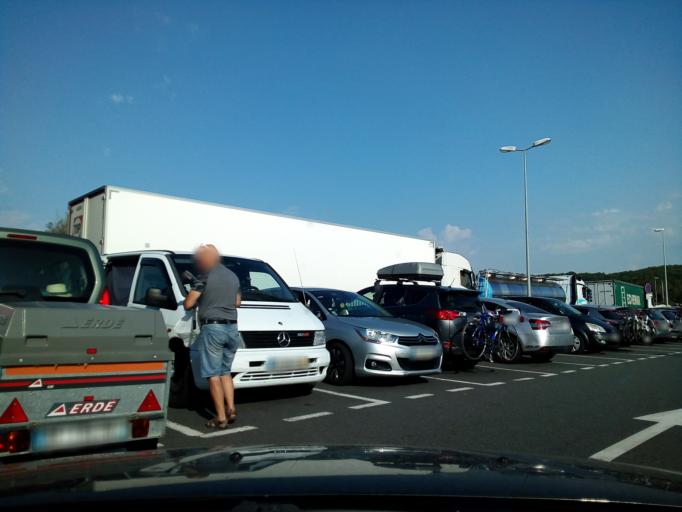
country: FR
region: Auvergne
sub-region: Departement de l'Allier
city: Doyet
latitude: 46.3552
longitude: 2.8011
